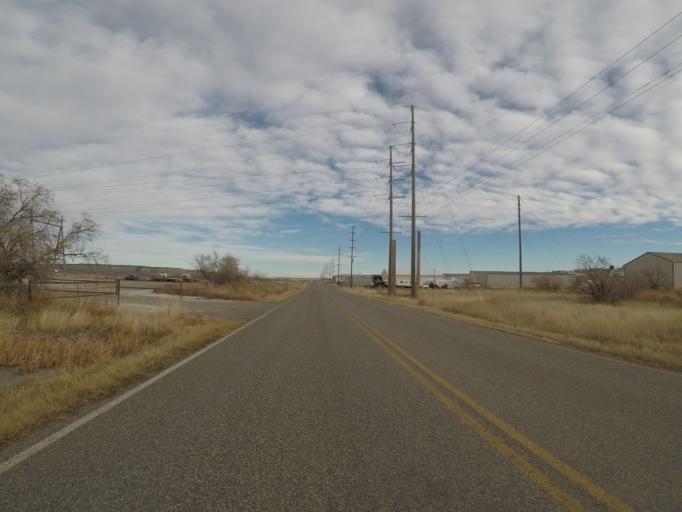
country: US
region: Montana
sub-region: Yellowstone County
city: Laurel
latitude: 45.7840
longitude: -108.7167
